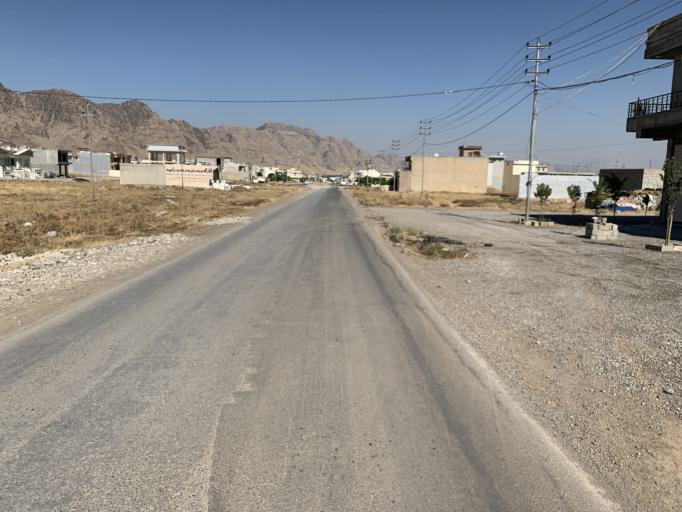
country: IQ
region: As Sulaymaniyah
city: Raniye
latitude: 36.2601
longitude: 44.8597
